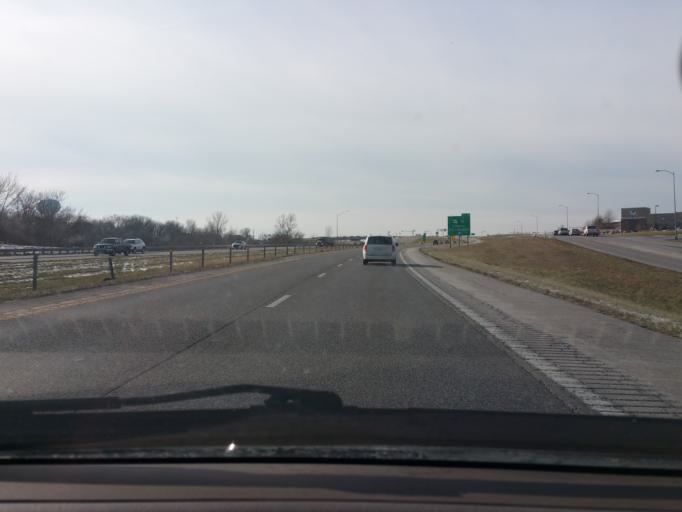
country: US
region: Missouri
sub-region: Clay County
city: Liberty
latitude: 39.2687
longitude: -94.4389
